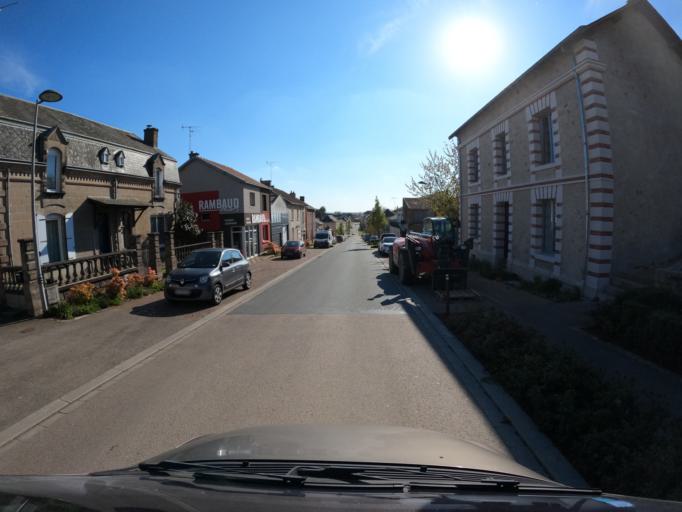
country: FR
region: Pays de la Loire
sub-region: Departement de la Vendee
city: Mortagne-sur-Sevre
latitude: 46.9952
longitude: -0.9474
